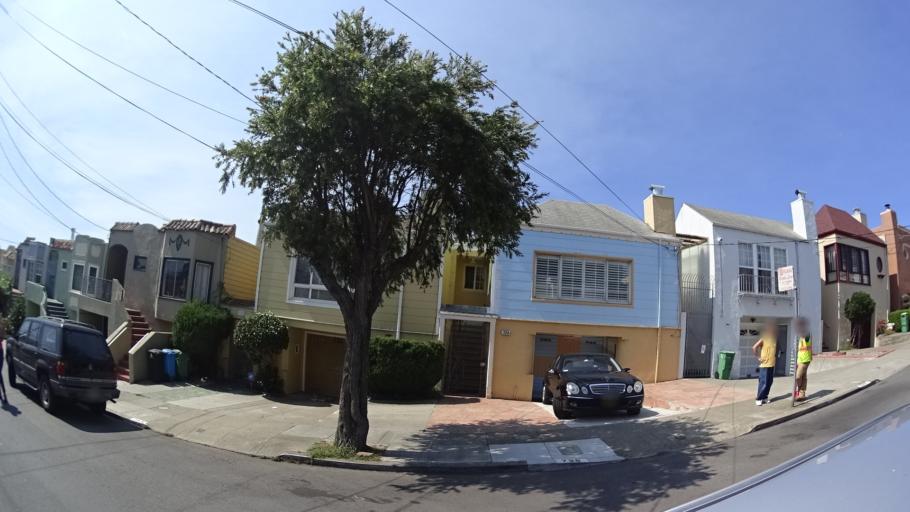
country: US
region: California
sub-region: San Mateo County
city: Daly City
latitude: 37.7173
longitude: -122.4561
